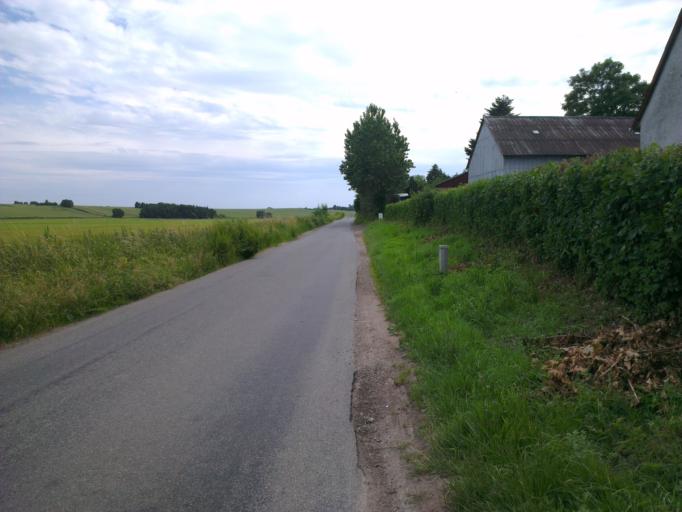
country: DK
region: Capital Region
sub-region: Frederikssund Kommune
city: Skibby
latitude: 55.7564
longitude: 12.0129
